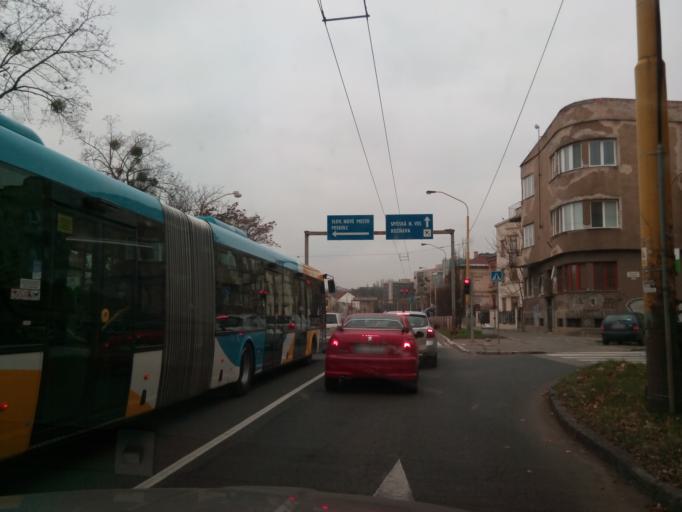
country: SK
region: Kosicky
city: Kosice
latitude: 48.7164
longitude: 21.2554
